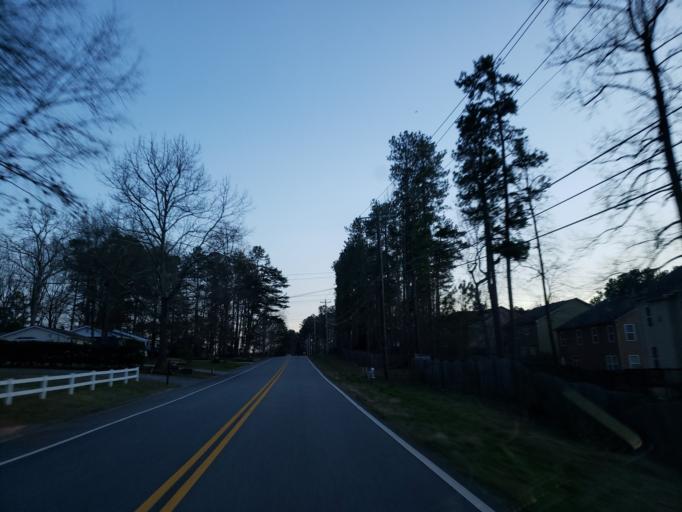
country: US
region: Georgia
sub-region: Cobb County
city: Kennesaw
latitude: 33.9977
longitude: -84.6345
